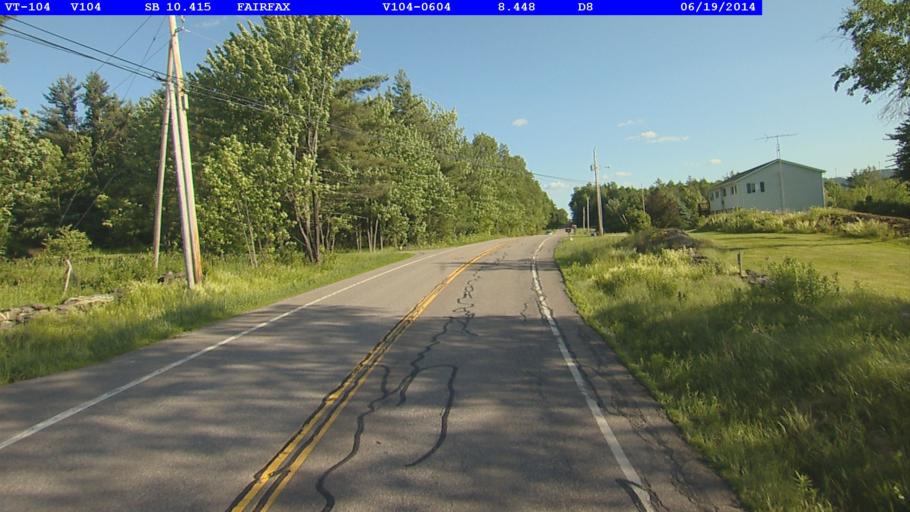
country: US
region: Vermont
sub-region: Chittenden County
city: Milton
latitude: 44.7063
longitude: -73.0364
